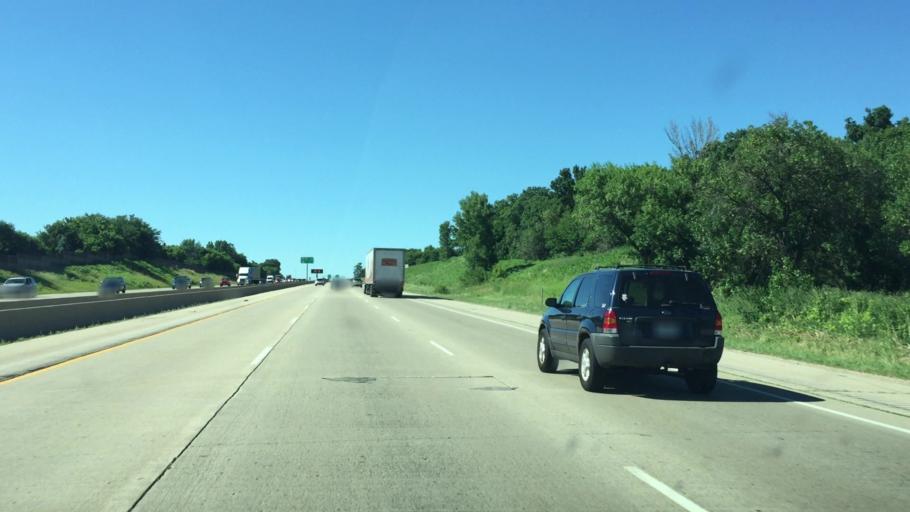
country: US
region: Wisconsin
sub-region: Dane County
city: Monona
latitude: 43.0749
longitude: -89.2805
